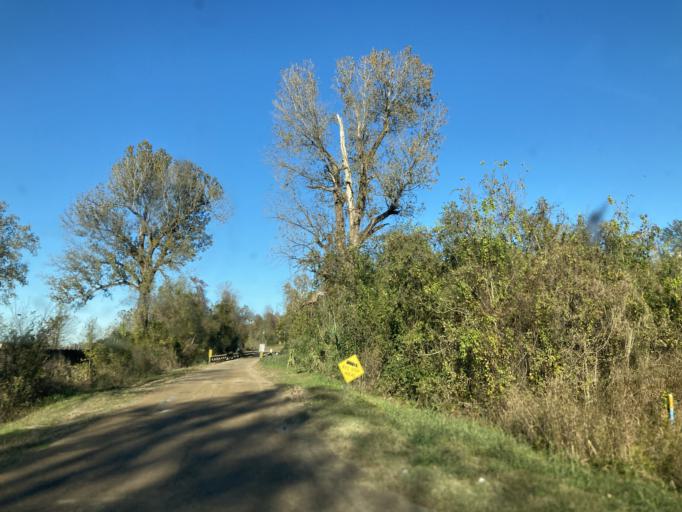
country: US
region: Mississippi
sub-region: Yazoo County
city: Yazoo City
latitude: 32.8151
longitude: -90.4497
